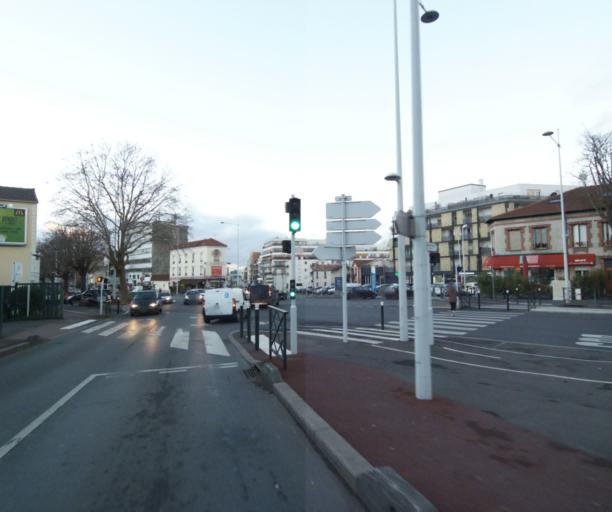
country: FR
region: Ile-de-France
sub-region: Departement des Hauts-de-Seine
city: Nanterre
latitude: 48.8862
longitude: 2.2097
